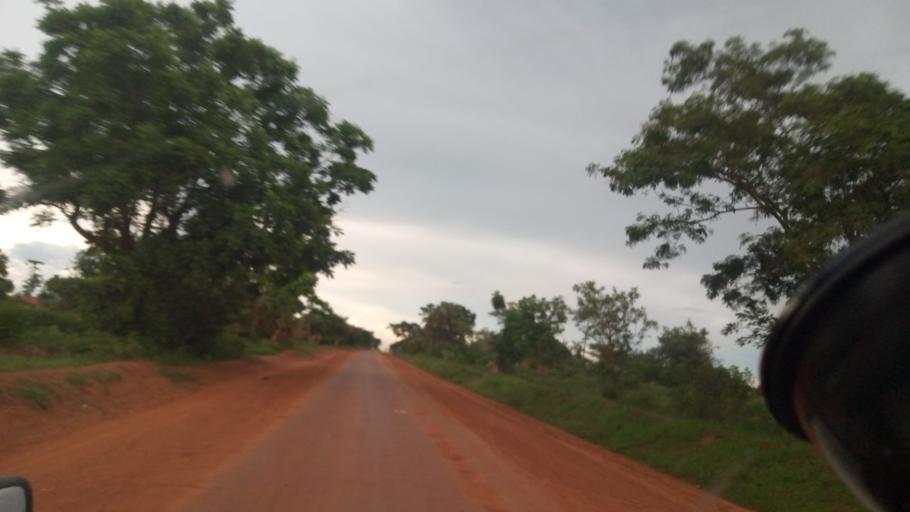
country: UG
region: Northern Region
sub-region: Kole District
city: Kole
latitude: 2.4727
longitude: 32.9363
